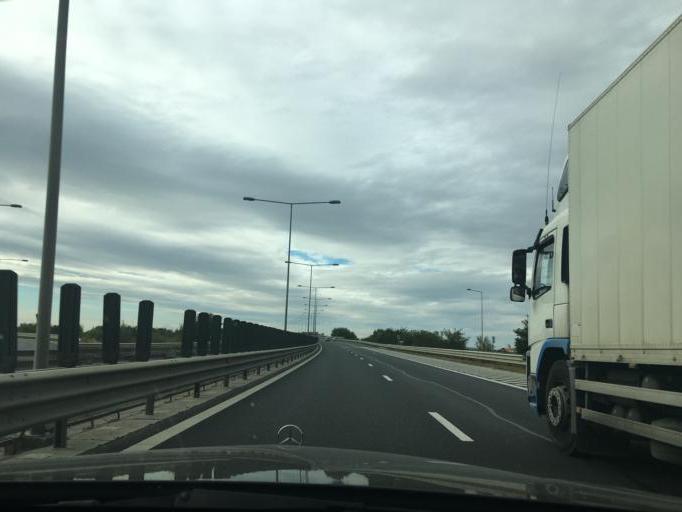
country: RO
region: Sibiu
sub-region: Comuna Selimbar
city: Selimbar
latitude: 45.7984
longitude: 24.1919
